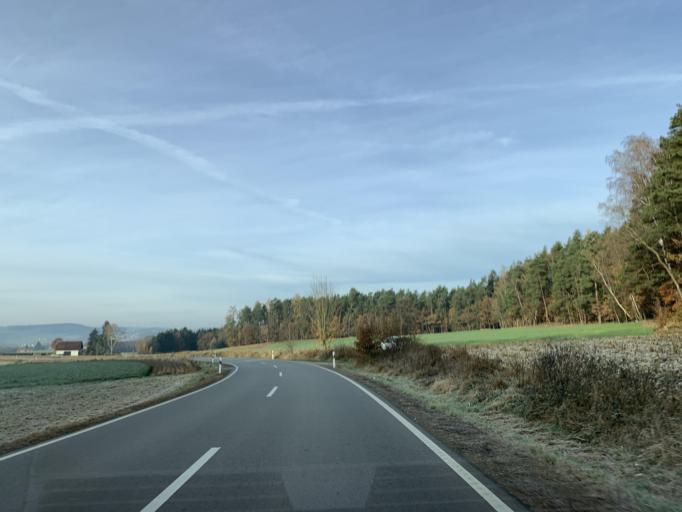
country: DE
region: Bavaria
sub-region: Upper Palatinate
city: Neunburg vorm Wald
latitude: 49.3555
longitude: 12.4168
